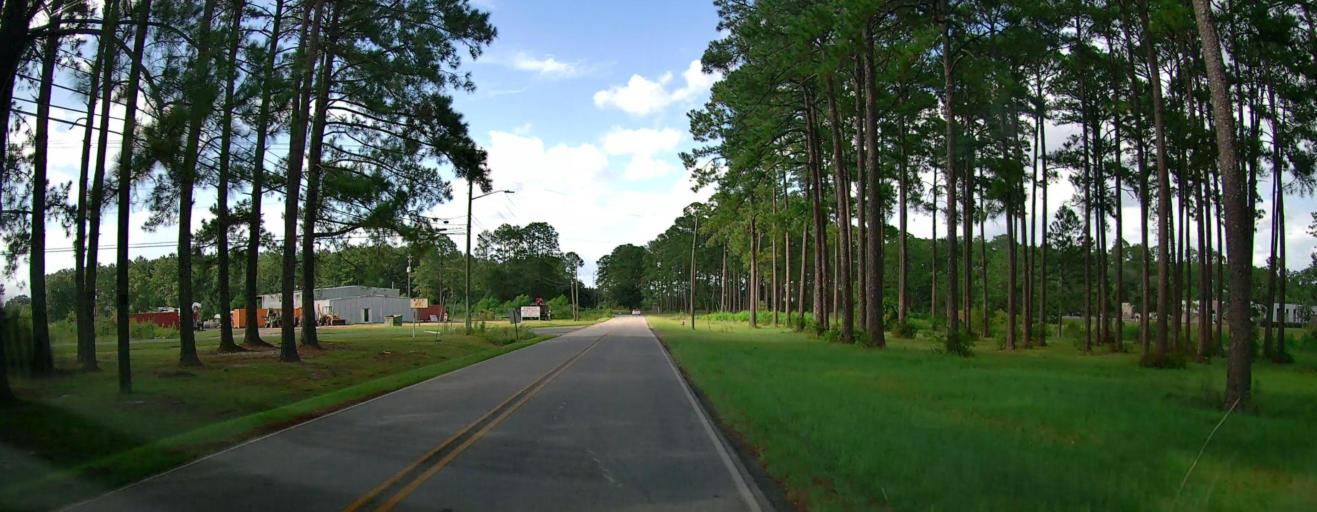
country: US
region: Georgia
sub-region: Coffee County
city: Douglas
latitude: 31.4951
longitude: -82.8589
